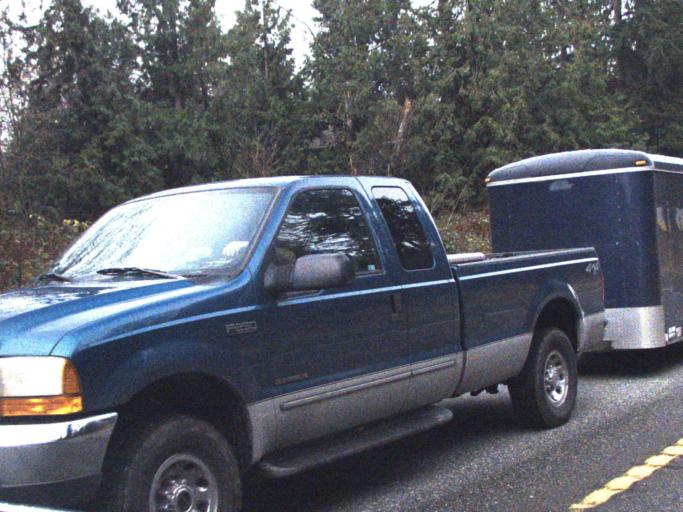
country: US
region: Washington
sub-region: Snohomish County
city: Fobes Hill
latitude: 47.9594
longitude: -122.1018
